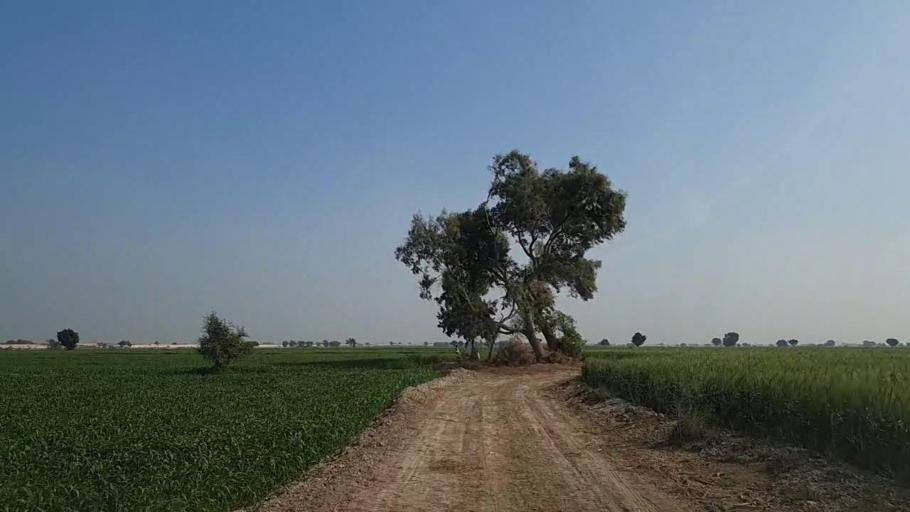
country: PK
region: Sindh
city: Moro
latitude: 26.6800
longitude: 67.9368
